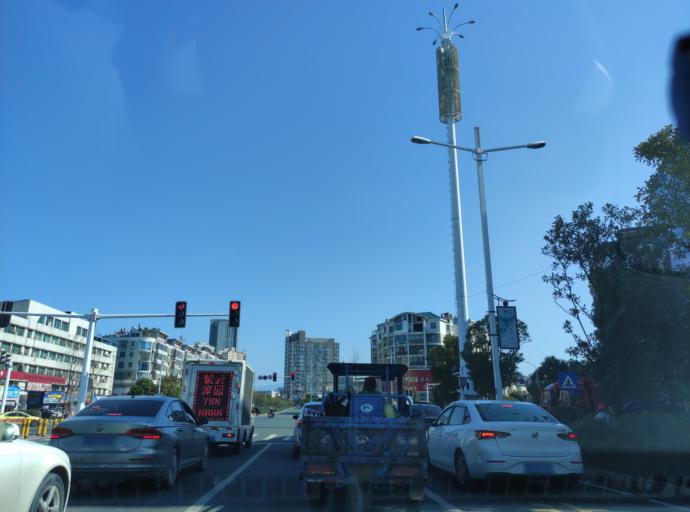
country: CN
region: Jiangxi Sheng
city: Pingxiang
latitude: 27.6525
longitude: 113.8632
